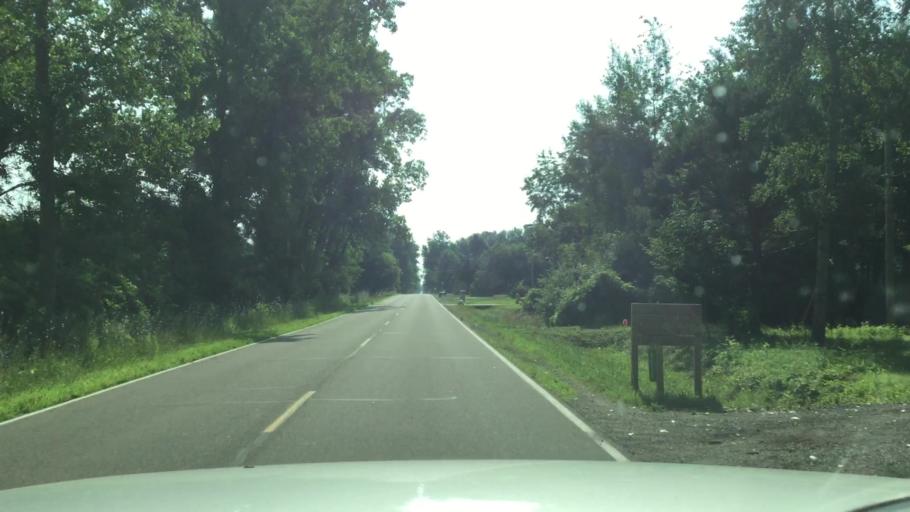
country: US
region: Michigan
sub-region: Genesee County
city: Montrose
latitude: 43.1333
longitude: -83.8530
